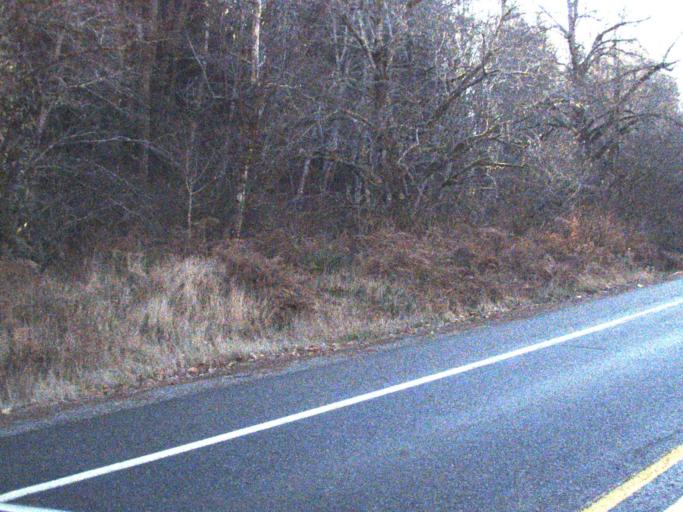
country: US
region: Washington
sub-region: Snohomish County
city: Darrington
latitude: 48.5833
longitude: -121.4023
